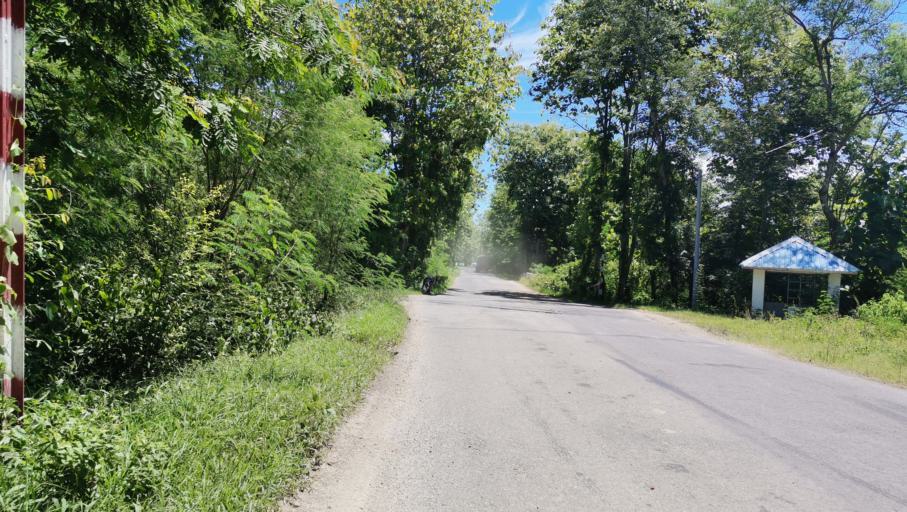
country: MM
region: Bago
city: Pyay
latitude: 18.7812
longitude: 95.1549
